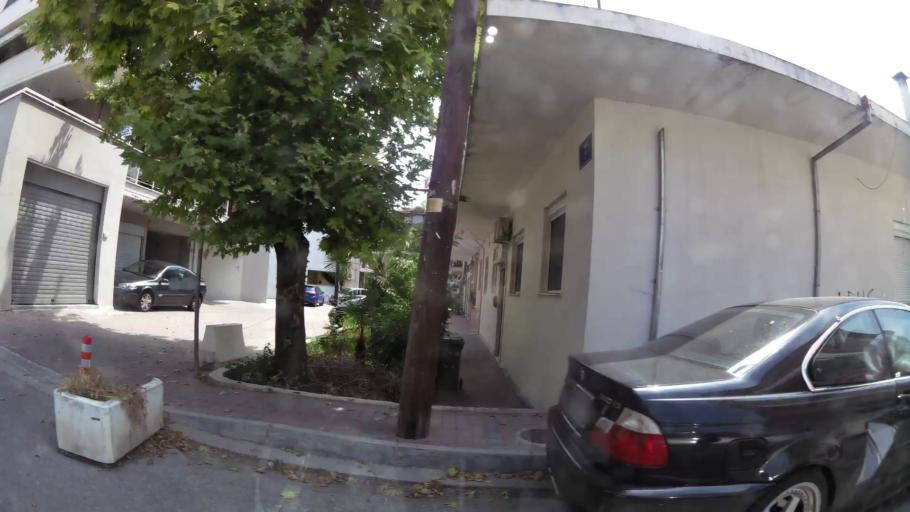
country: GR
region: Central Macedonia
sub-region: Nomos Pierias
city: Katerini
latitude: 40.2705
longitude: 22.5032
